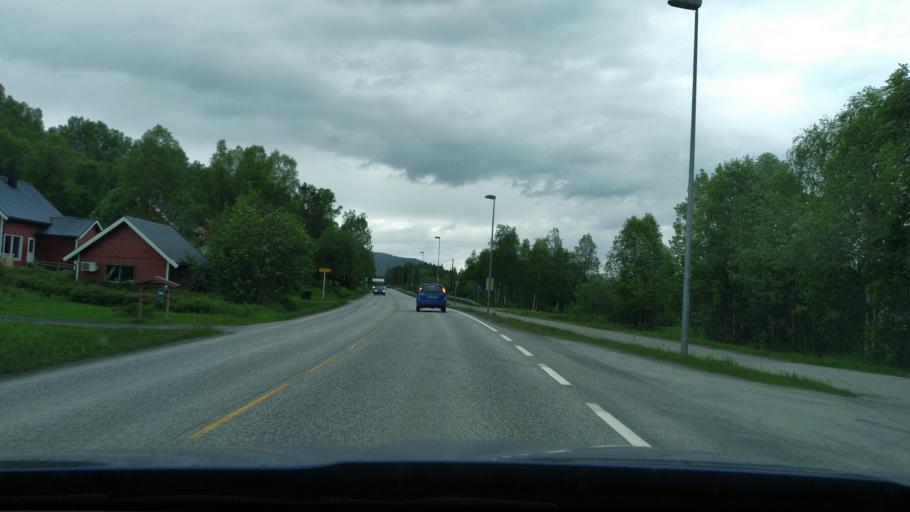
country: NO
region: Troms
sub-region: Malselv
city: Moen
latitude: 69.0340
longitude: 18.5059
